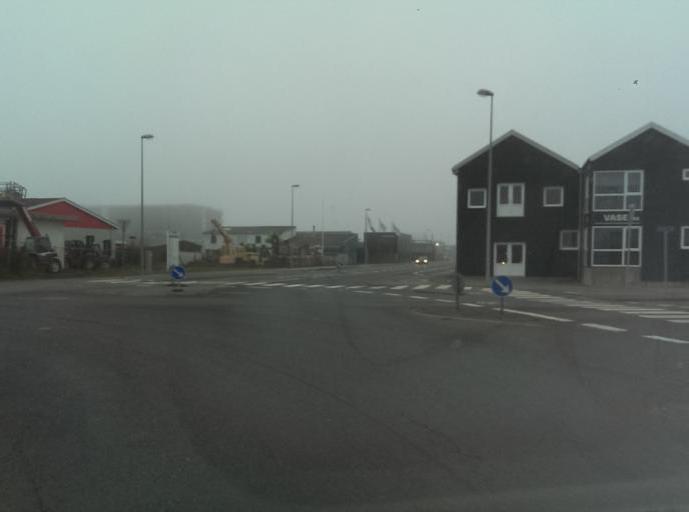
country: DK
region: South Denmark
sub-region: Esbjerg Kommune
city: Esbjerg
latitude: 55.4725
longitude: 8.4312
